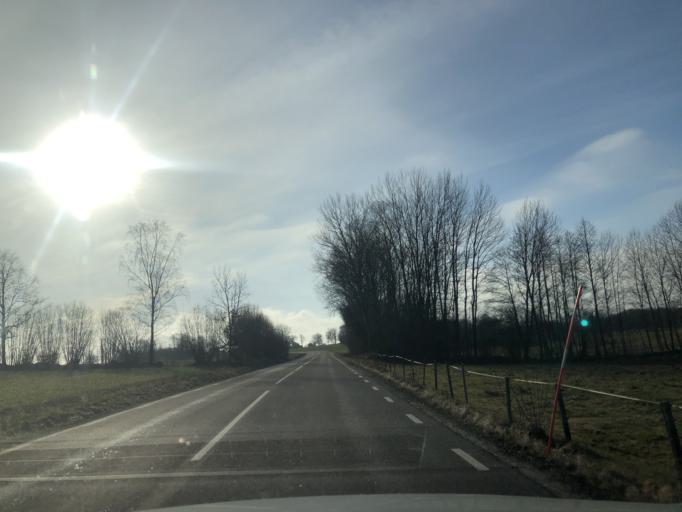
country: SE
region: Vaestra Goetaland
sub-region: Ulricehamns Kommun
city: Ulricehamn
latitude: 57.6707
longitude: 13.4022
